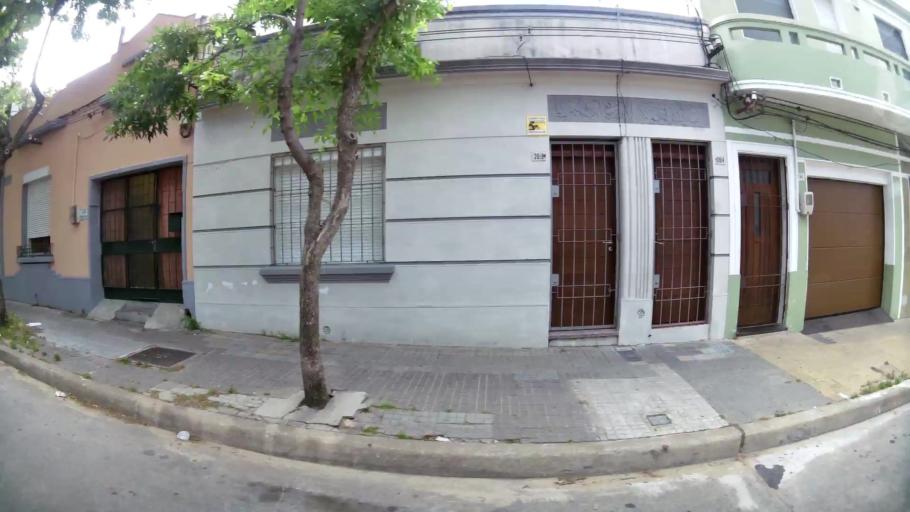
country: UY
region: Montevideo
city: Montevideo
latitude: -34.8831
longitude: -56.1357
